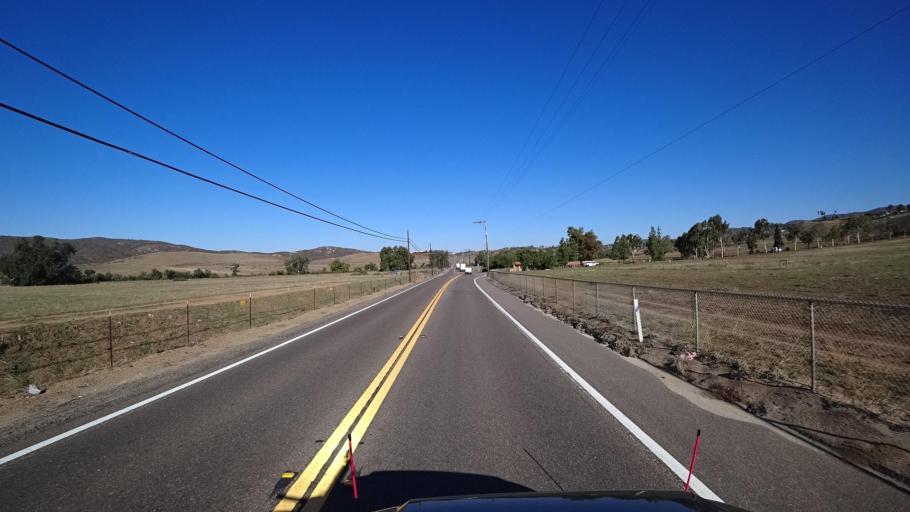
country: US
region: California
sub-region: San Diego County
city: Jamul
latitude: 32.6940
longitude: -116.8580
